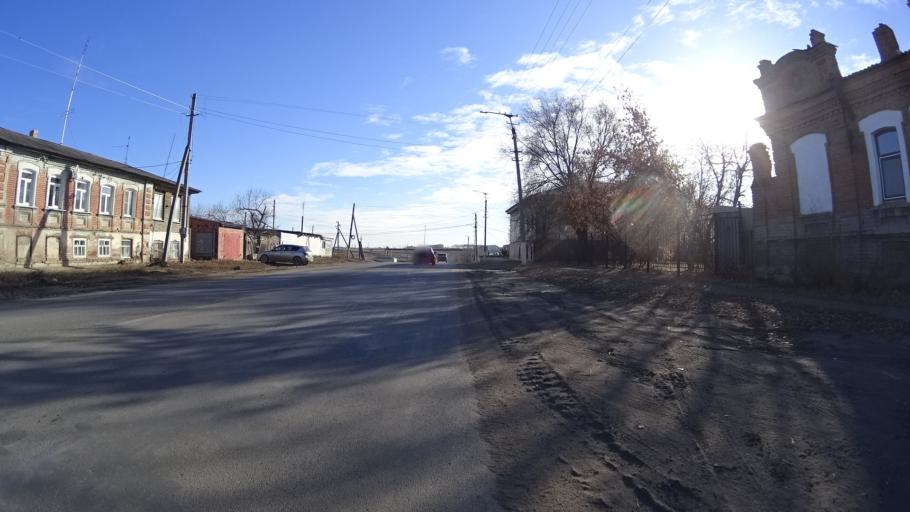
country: RU
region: Chelyabinsk
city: Troitsk
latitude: 54.0778
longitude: 61.5541
